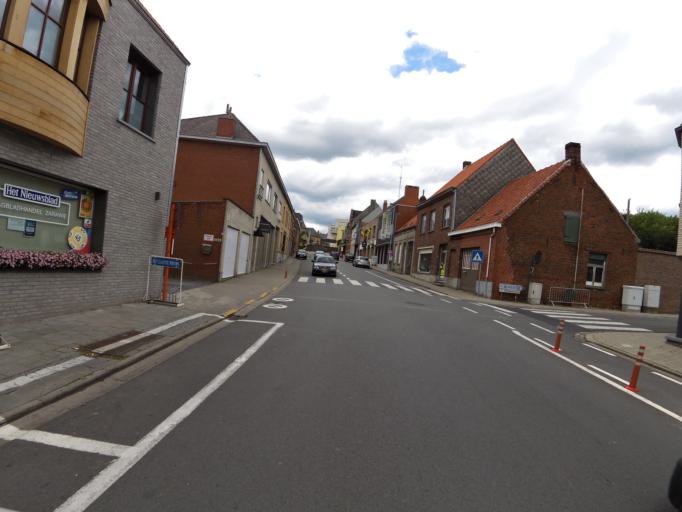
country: BE
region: Flanders
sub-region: Provincie West-Vlaanderen
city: Hooglede
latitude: 50.9768
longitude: 3.0836
